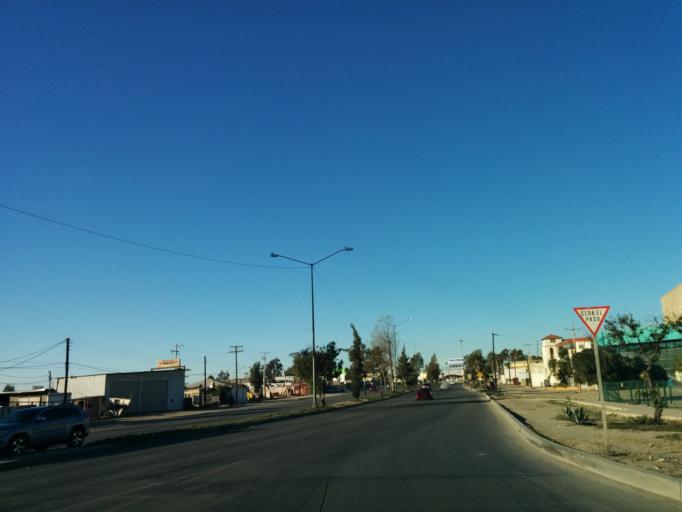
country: MX
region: Baja California
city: Tijuana
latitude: 32.5440
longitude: -116.9475
